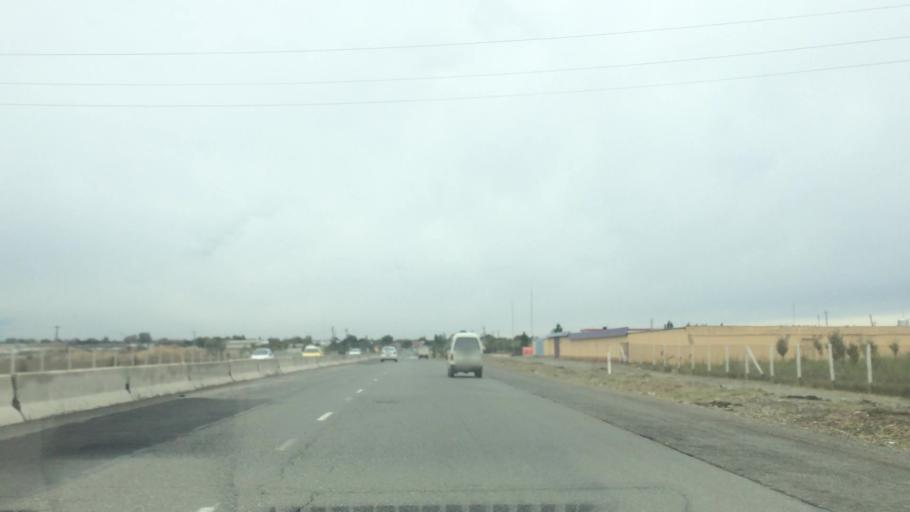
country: UZ
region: Samarqand
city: Bulung'ur
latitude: 39.7754
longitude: 67.2849
